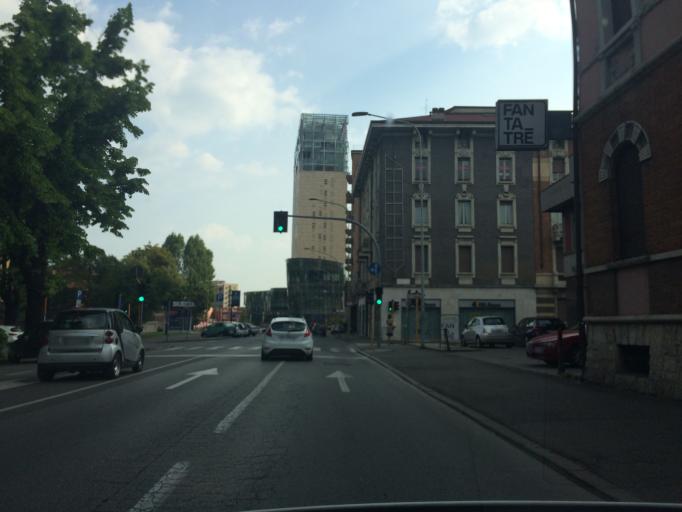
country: IT
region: Lombardy
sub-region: Provincia di Brescia
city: Brescia
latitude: 45.5381
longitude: 10.2098
